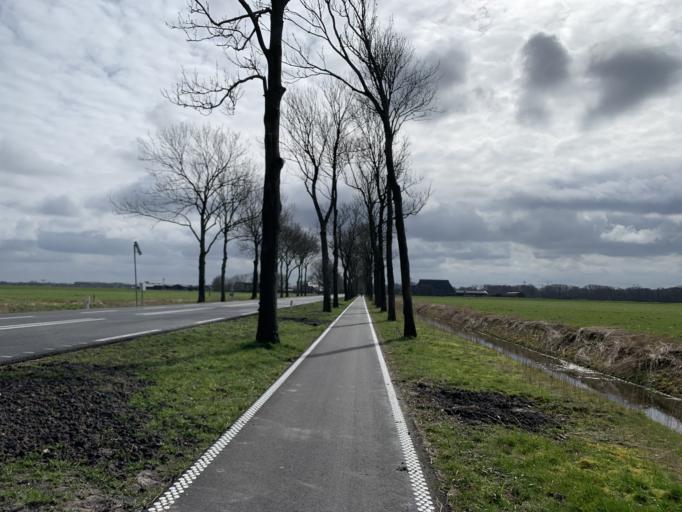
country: NL
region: Groningen
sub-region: Gemeente Groningen
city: Korrewegwijk
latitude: 53.2565
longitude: 6.5410
